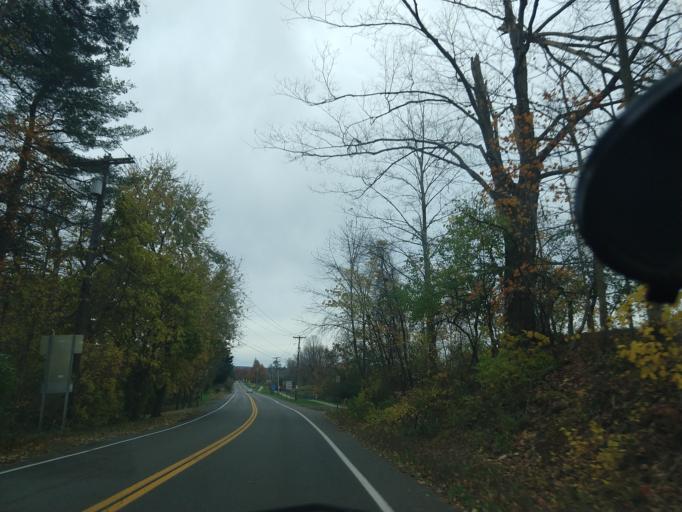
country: US
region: New York
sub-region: Tompkins County
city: Cayuga Heights
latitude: 42.4608
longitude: -76.4758
